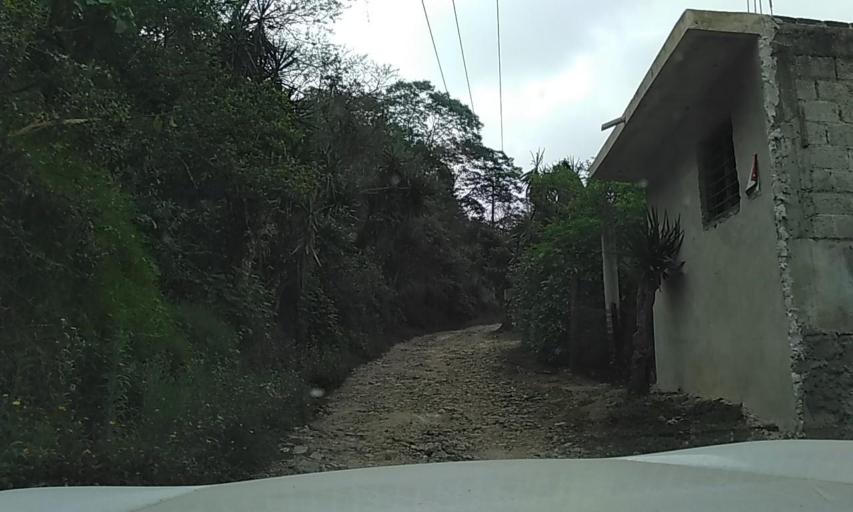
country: MX
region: Veracruz
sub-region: Xalapa
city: Xalapa de Enriquez
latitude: 19.5016
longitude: -96.9199
